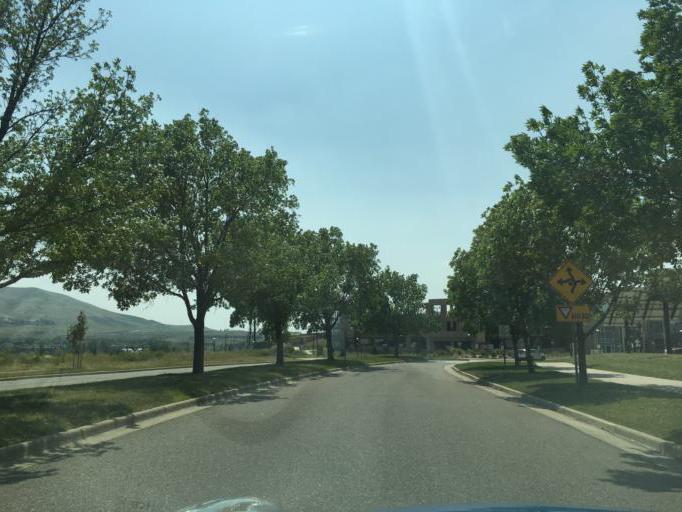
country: US
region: Colorado
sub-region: Jefferson County
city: West Pleasant View
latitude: 39.7281
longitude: -105.1992
